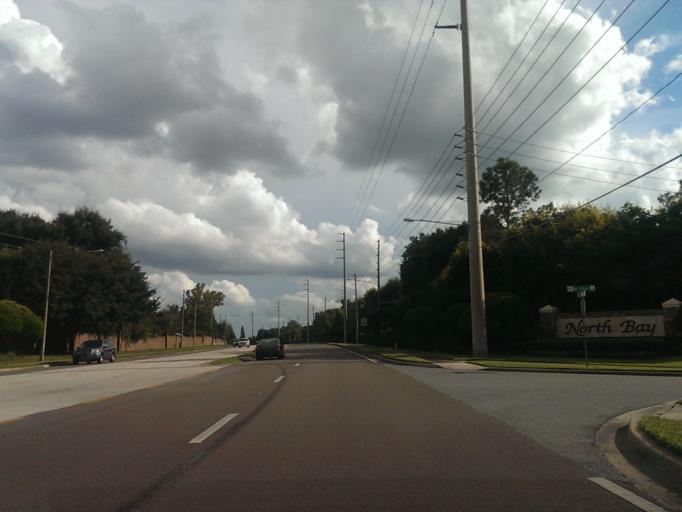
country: US
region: Florida
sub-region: Orange County
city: Bay Hill
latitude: 28.4762
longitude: -81.5083
